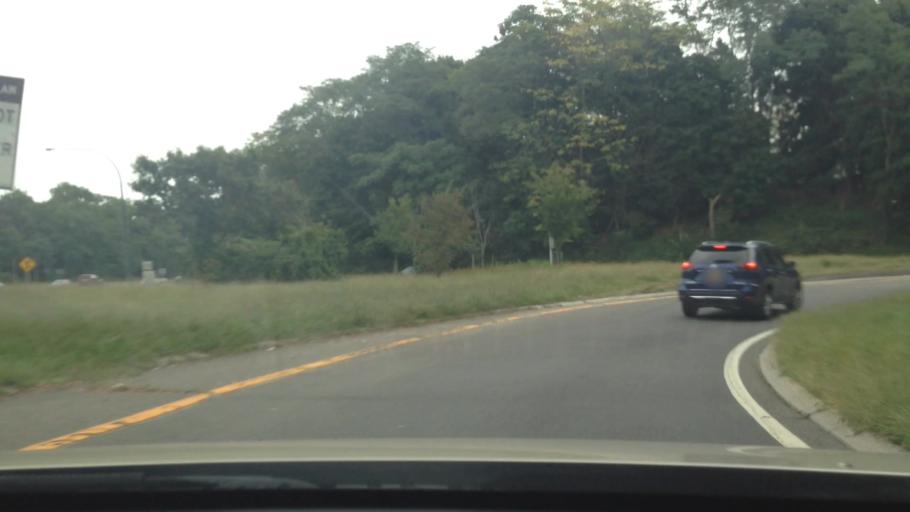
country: US
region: New York
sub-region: Nassau County
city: Roslyn Heights
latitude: 40.7816
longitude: -73.6471
